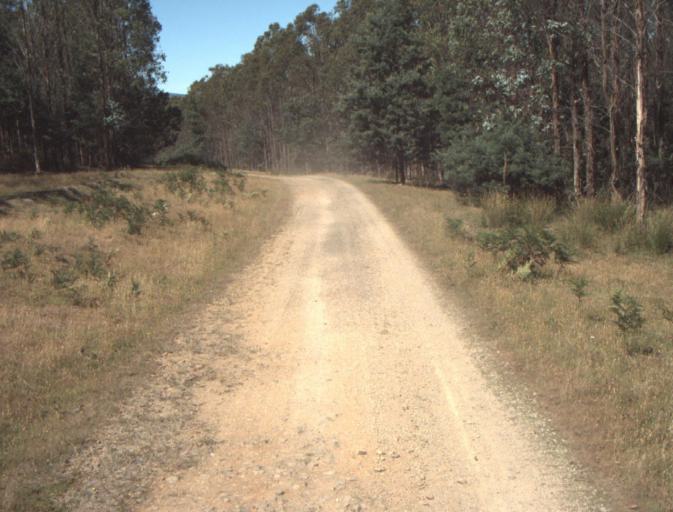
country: AU
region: Tasmania
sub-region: Dorset
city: Scottsdale
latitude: -41.2637
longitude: 147.3503
